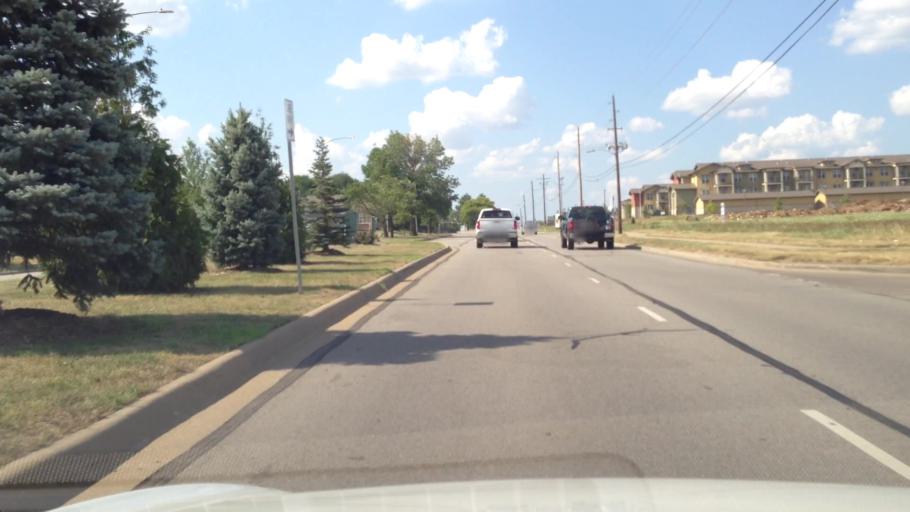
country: US
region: Kansas
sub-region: Johnson County
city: Olathe
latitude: 38.9145
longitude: -94.7973
